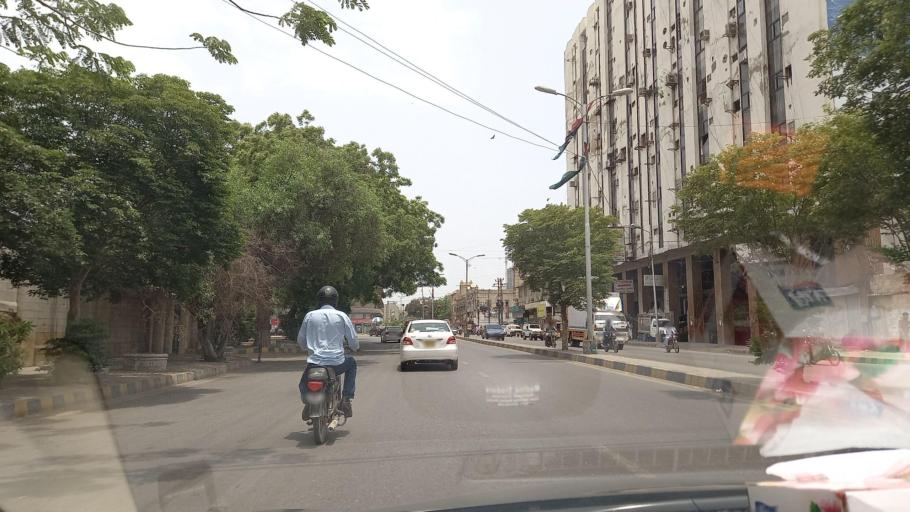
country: PK
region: Sindh
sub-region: Karachi District
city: Karachi
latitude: 24.8519
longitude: 67.0294
